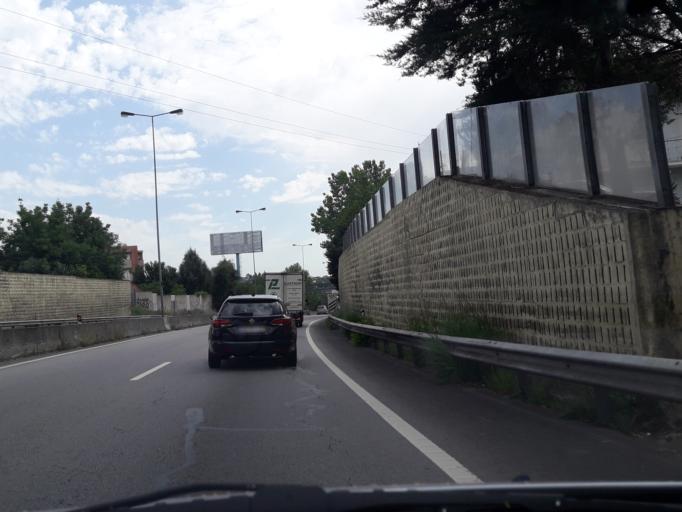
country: PT
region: Braga
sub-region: Braga
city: Braga
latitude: 41.5408
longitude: -8.4416
